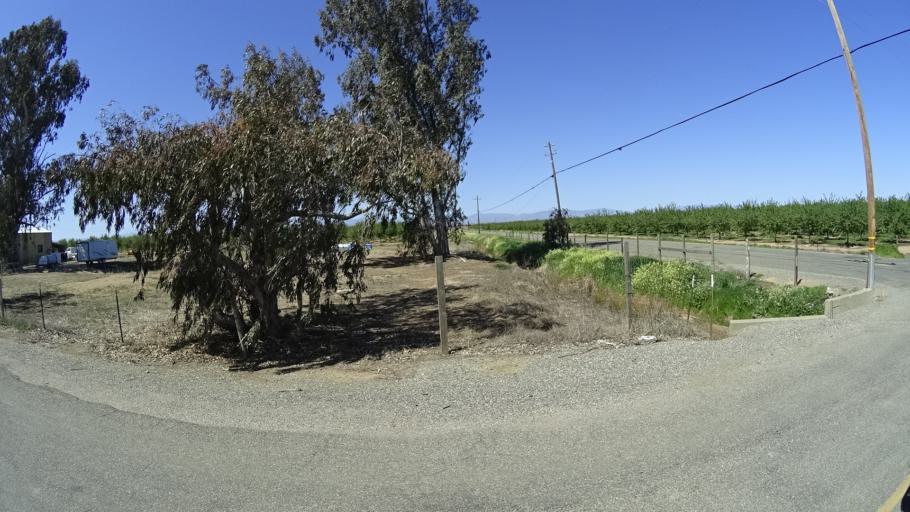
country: US
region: California
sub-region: Glenn County
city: Orland
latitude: 39.6681
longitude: -122.2531
